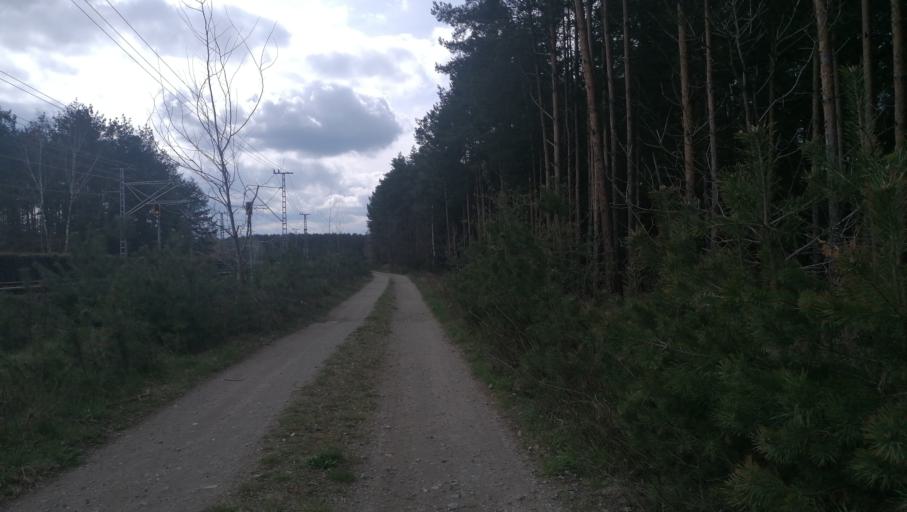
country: DE
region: Brandenburg
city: Cottbus
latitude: 51.6861
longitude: 14.3390
